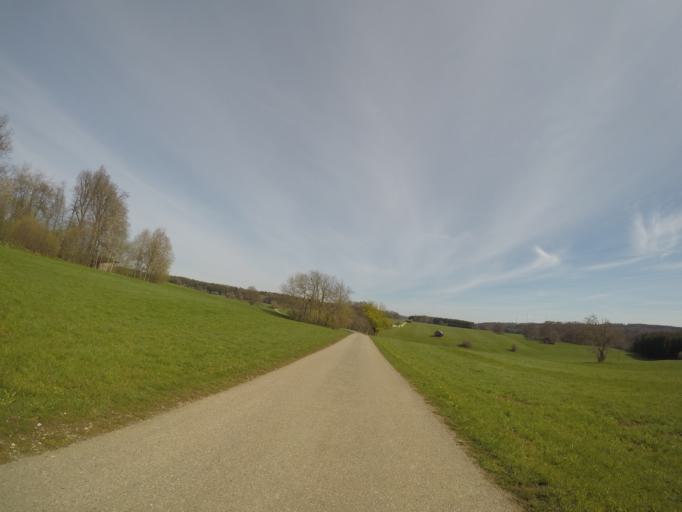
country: DE
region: Baden-Wuerttemberg
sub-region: Tuebingen Region
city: Laichingen
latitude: 48.5111
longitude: 9.6782
